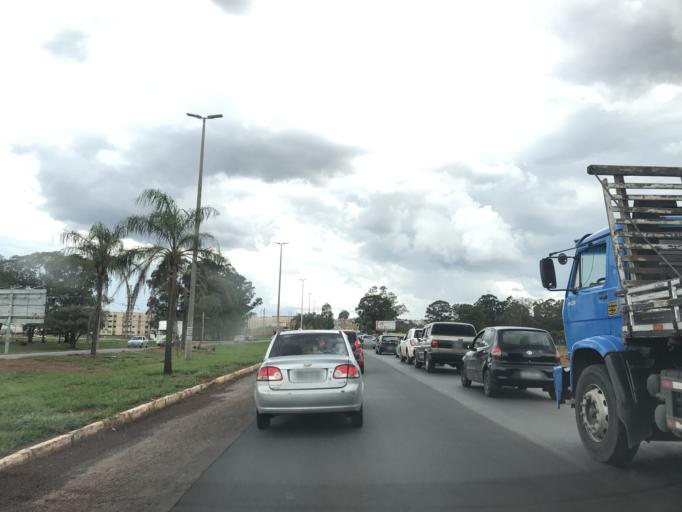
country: BR
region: Federal District
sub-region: Brasilia
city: Brasilia
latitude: -15.8883
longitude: -48.0585
